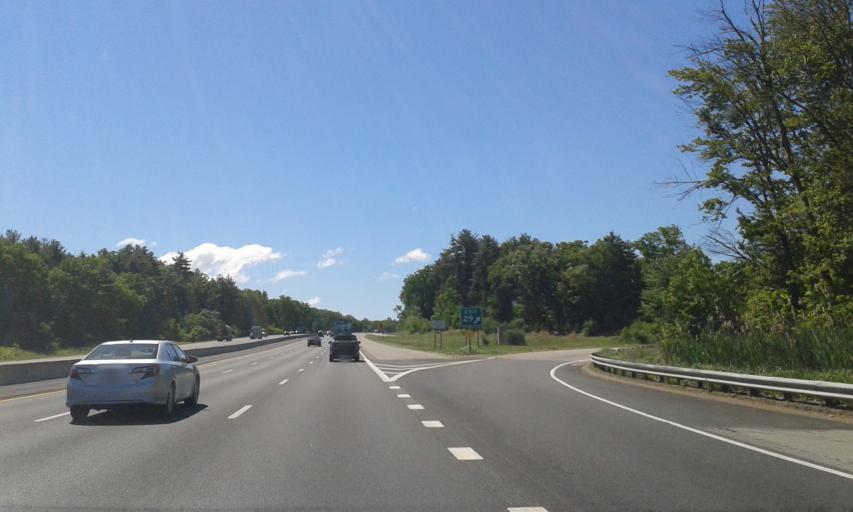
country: US
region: Massachusetts
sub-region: Middlesex County
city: Lowell
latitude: 42.5886
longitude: -71.3129
